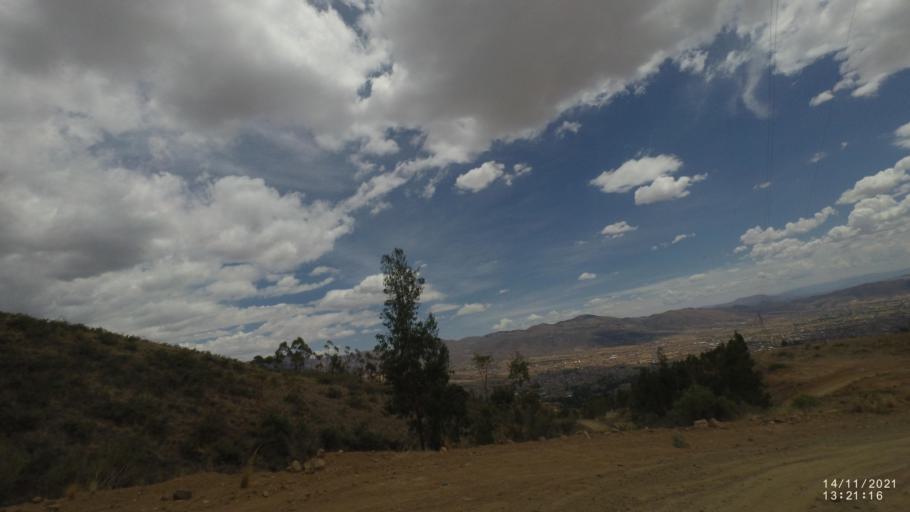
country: BO
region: Cochabamba
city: Colomi
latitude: -17.3754
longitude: -65.9822
